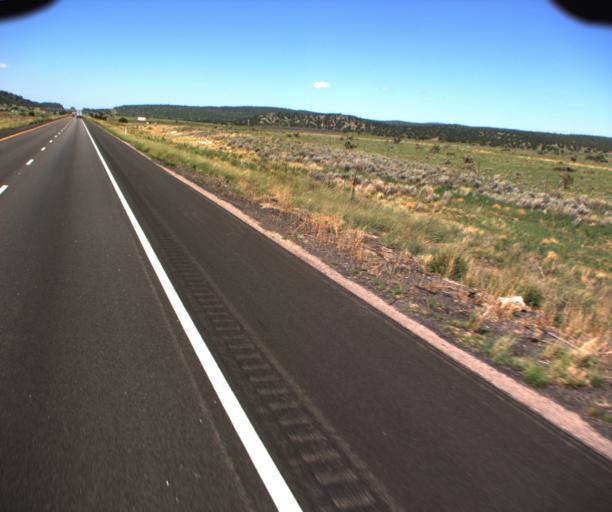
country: US
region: Arizona
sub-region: Mohave County
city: Peach Springs
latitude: 35.2593
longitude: -113.1661
